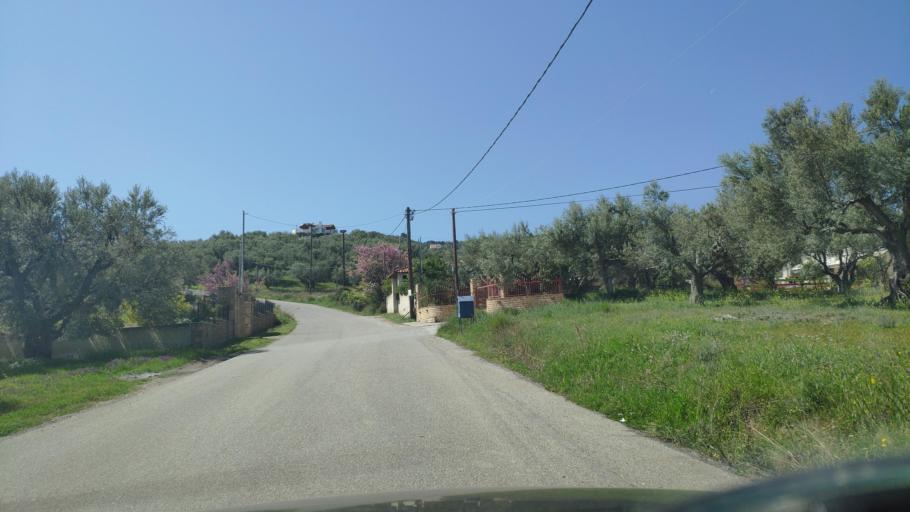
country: GR
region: West Greece
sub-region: Nomos Achaias
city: Aiyira
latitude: 38.1367
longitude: 22.3480
